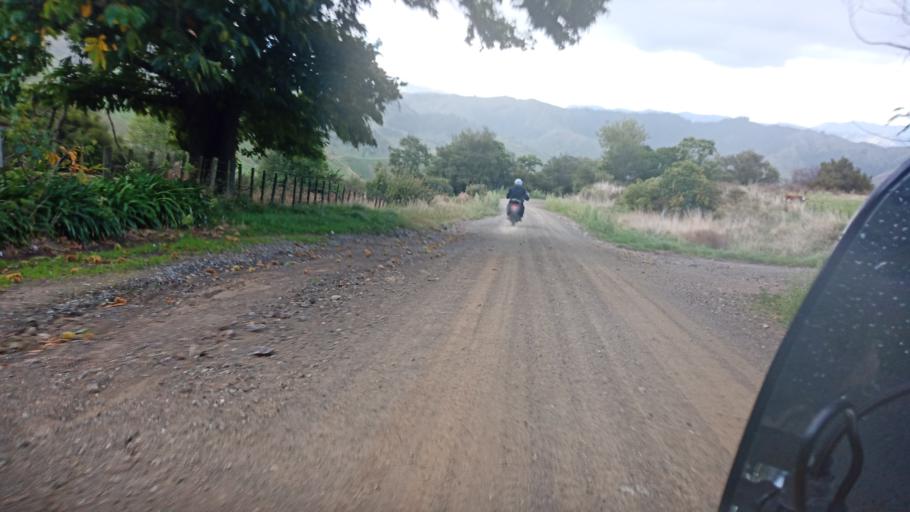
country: NZ
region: Gisborne
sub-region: Gisborne District
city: Gisborne
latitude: -38.4708
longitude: 177.6189
